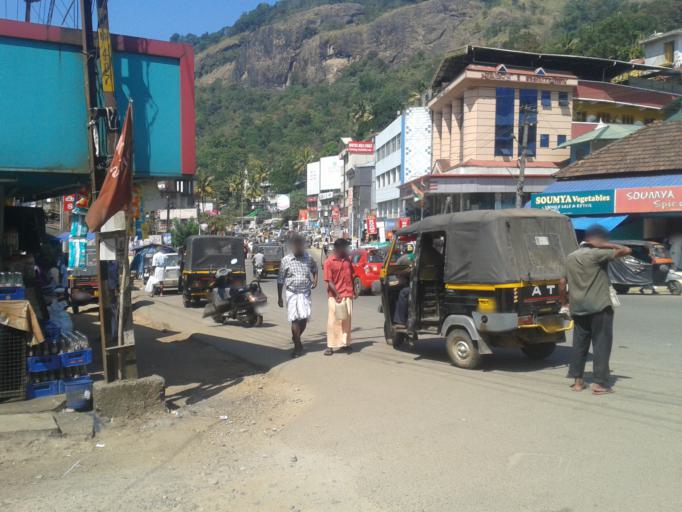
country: IN
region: Kerala
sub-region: Idukki
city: Munnar
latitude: 10.0142
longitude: 76.9549
